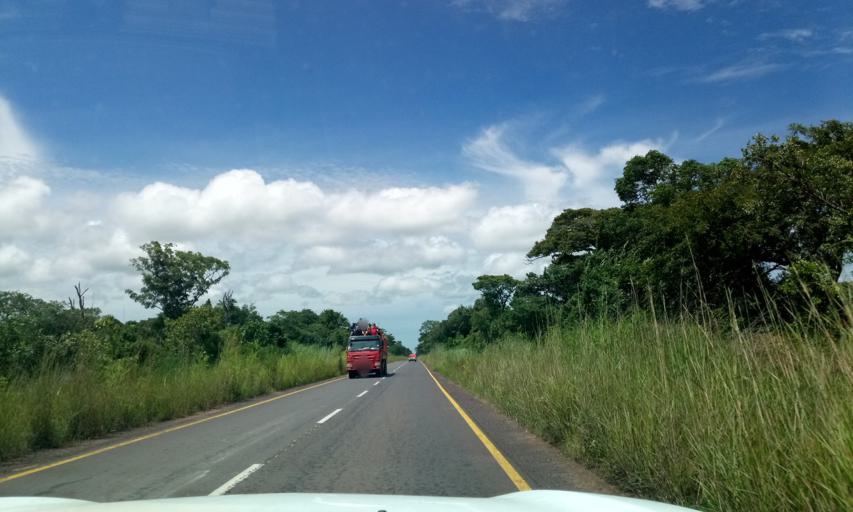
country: CD
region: Katanga
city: Lubumbashi
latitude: -11.1041
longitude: 27.9765
